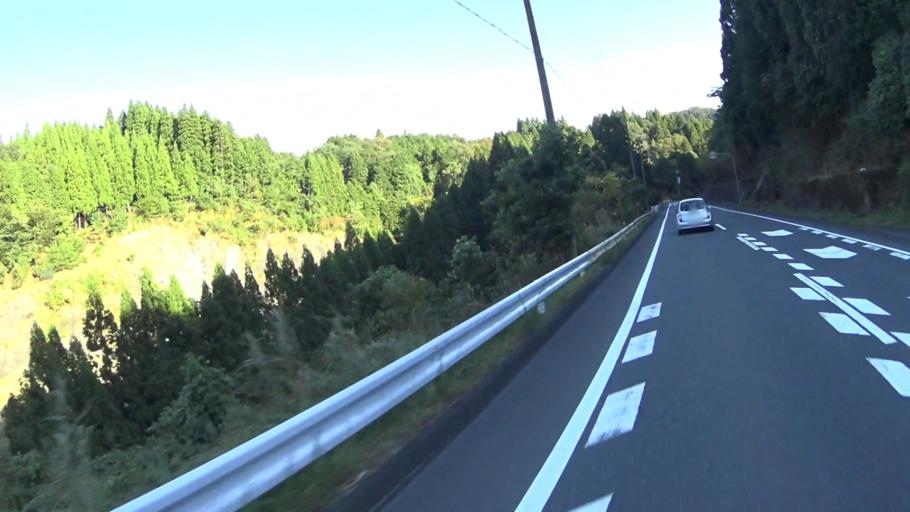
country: JP
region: Kyoto
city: Fukuchiyama
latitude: 35.3696
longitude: 135.1001
